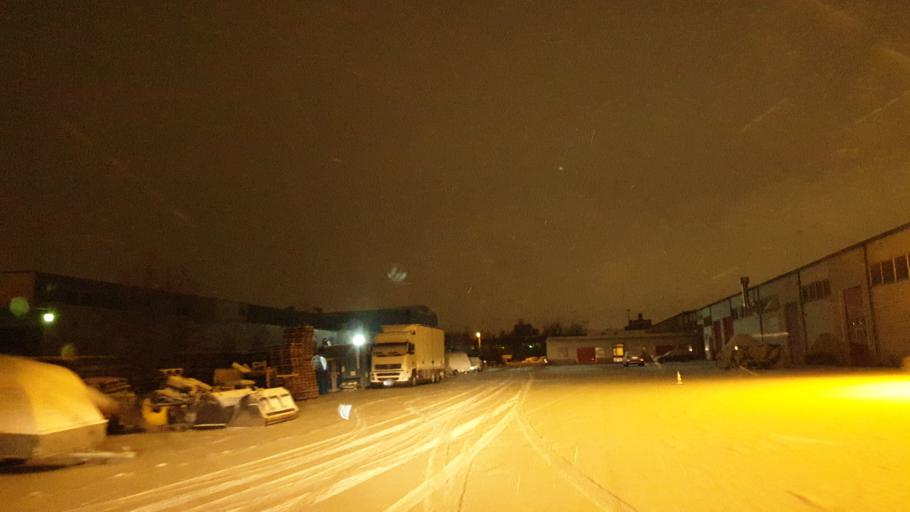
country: FI
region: Northern Ostrobothnia
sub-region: Oulu
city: Oulu
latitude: 64.9917
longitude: 25.4546
